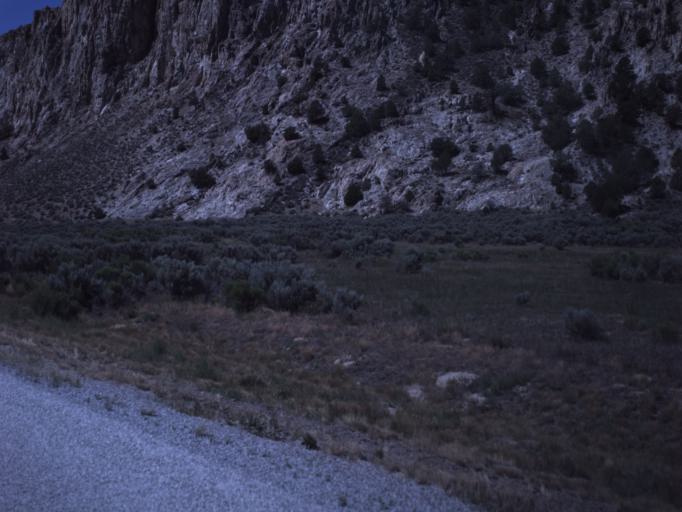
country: US
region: Utah
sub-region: Garfield County
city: Panguitch
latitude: 38.0322
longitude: -112.3570
